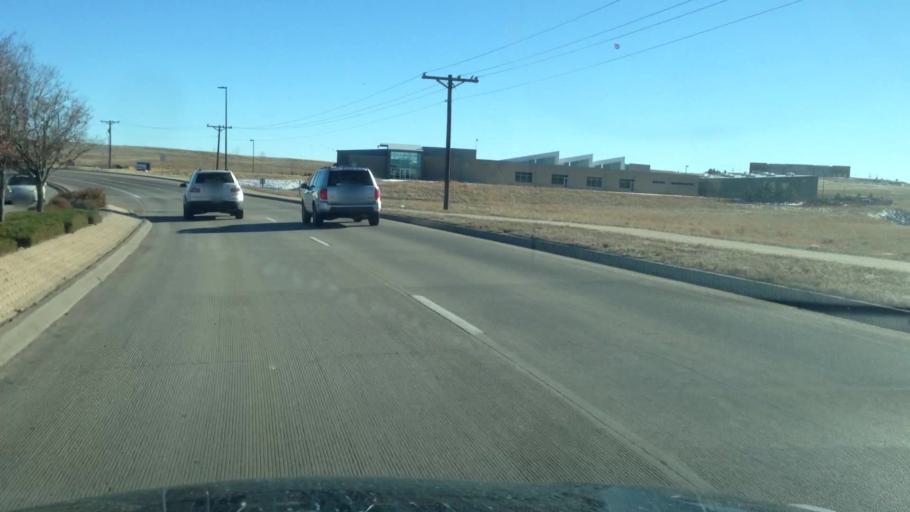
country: US
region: Colorado
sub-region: Arapahoe County
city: Dove Valley
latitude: 39.5836
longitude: -104.8144
